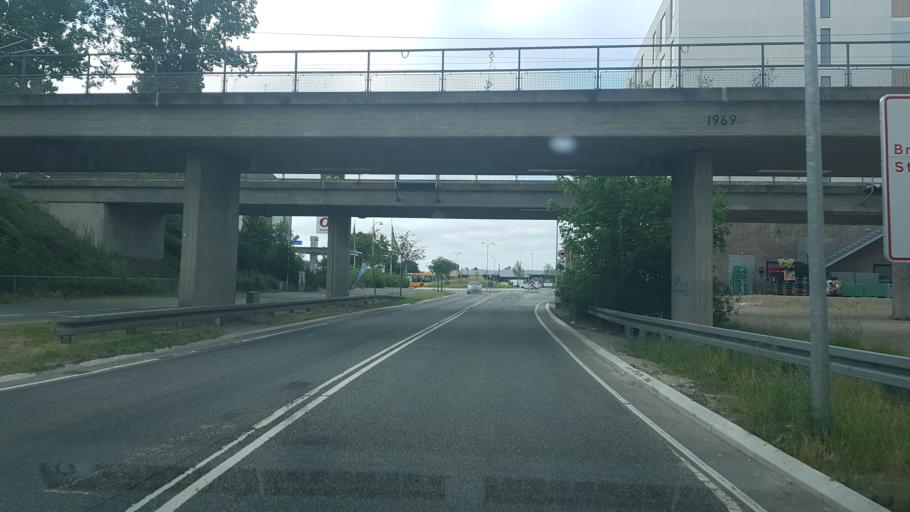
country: DK
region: Capital Region
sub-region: Vallensbaek Kommune
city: Vallensbaek
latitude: 55.6237
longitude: 12.3895
